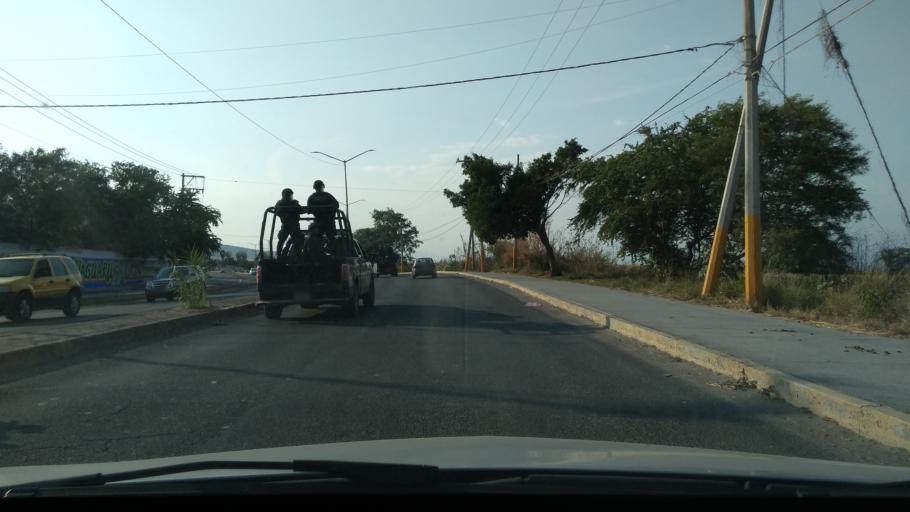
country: MX
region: Morelos
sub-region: Jojutla
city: Jojutla
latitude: 18.6191
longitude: -99.1922
